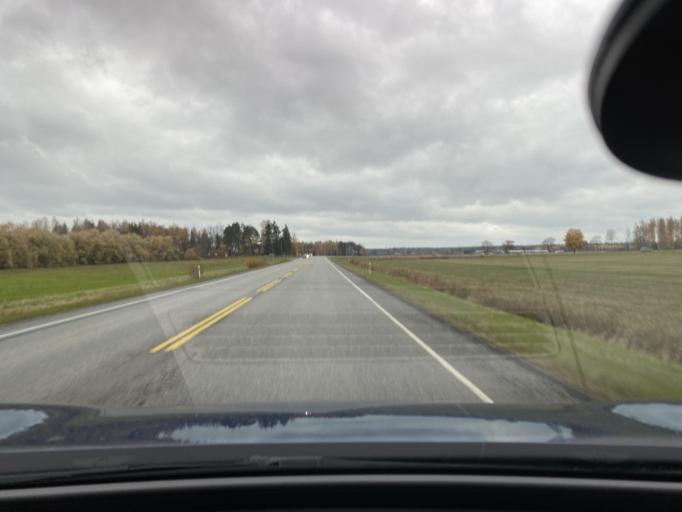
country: FI
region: Satakunta
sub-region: Rauma
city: Kiukainen
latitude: 61.1879
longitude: 22.0605
